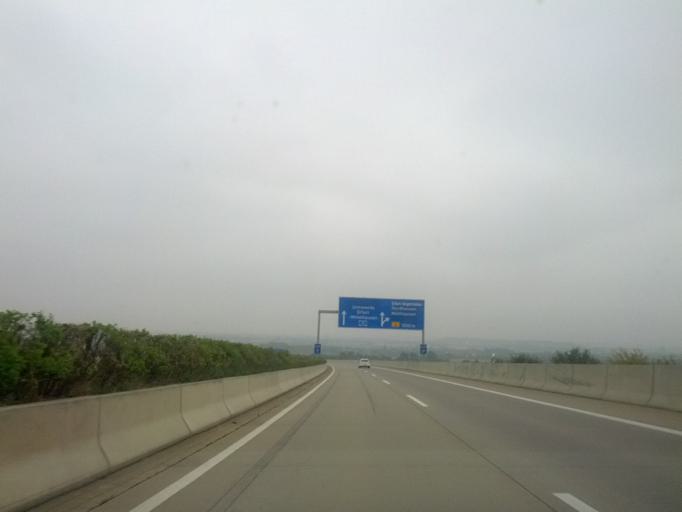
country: DE
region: Thuringia
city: Elxleben
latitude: 51.0122
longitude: 10.9590
